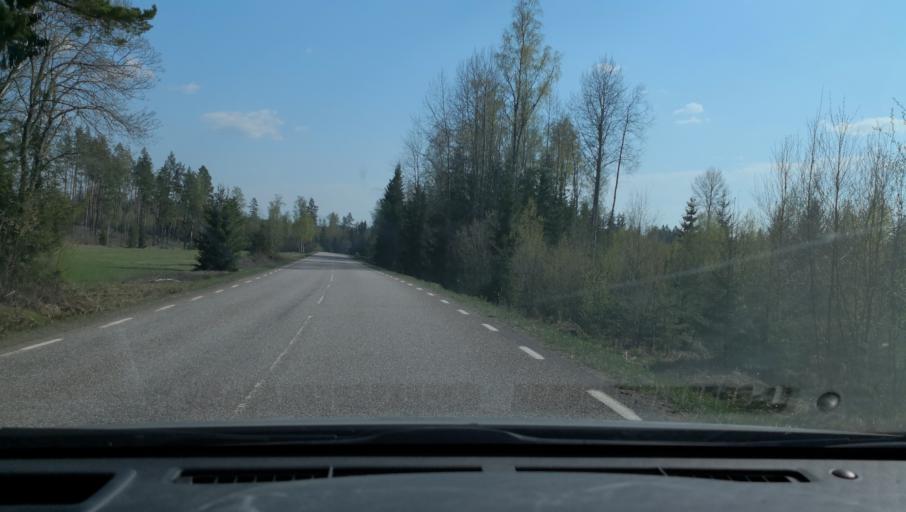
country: SE
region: Vaestmanland
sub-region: Sala Kommun
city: Sala
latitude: 60.0460
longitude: 16.6405
